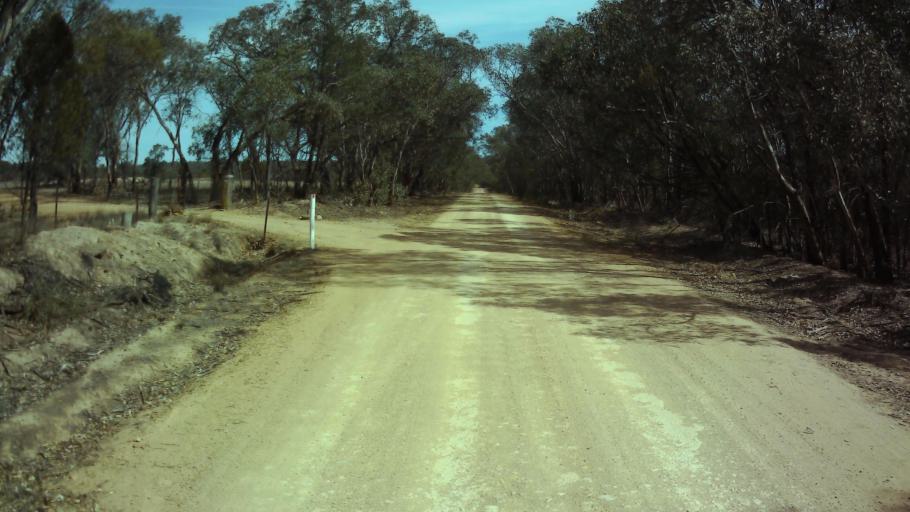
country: AU
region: New South Wales
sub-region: Weddin
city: Grenfell
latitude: -33.8764
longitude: 148.1492
